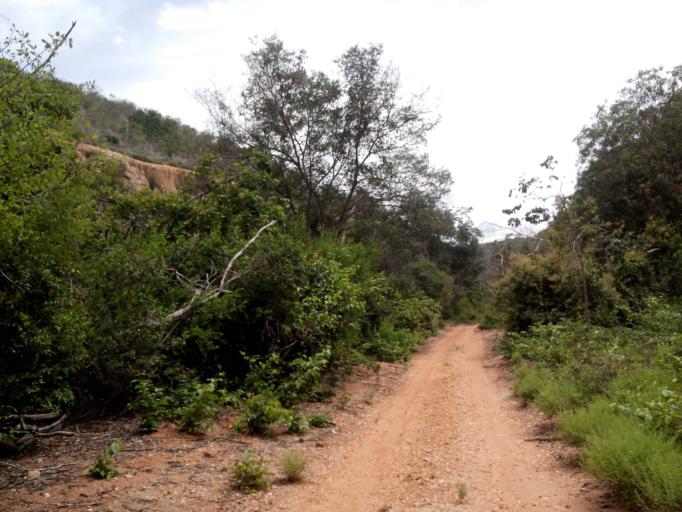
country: BR
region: Piaui
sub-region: Sao Raimundo Nonato
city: Sao Raimundo Nonato
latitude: -8.7742
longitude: -42.4818
